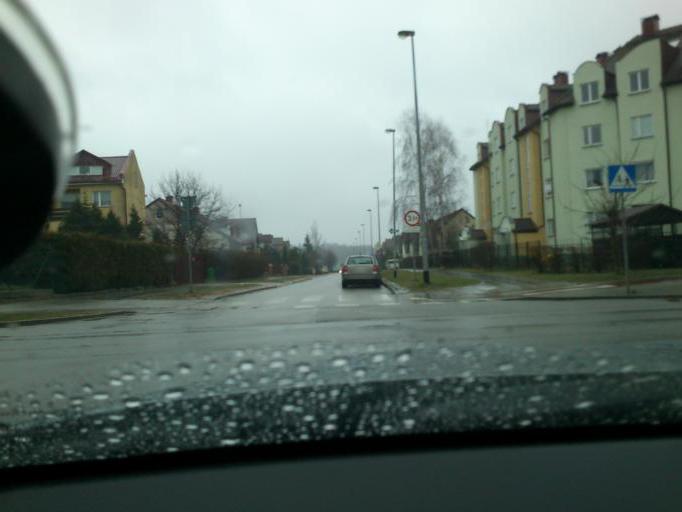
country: PL
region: Pomeranian Voivodeship
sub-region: Gdynia
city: Wielki Kack
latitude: 54.4245
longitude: 18.4786
